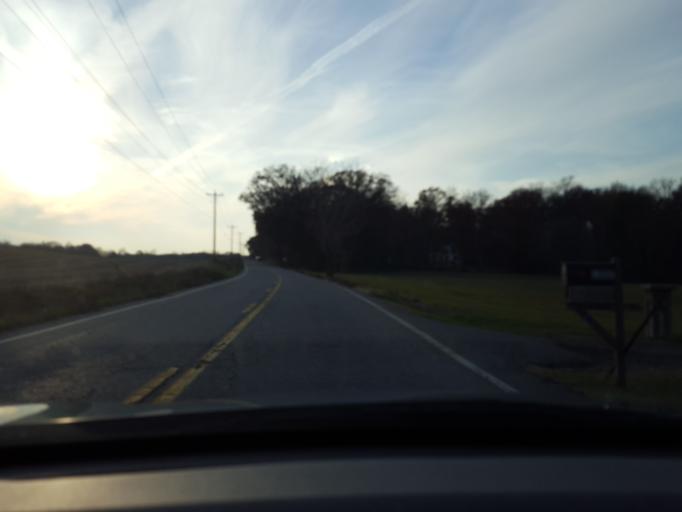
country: US
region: Maryland
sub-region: Charles County
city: Hughesville
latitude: 38.5319
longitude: -76.7902
